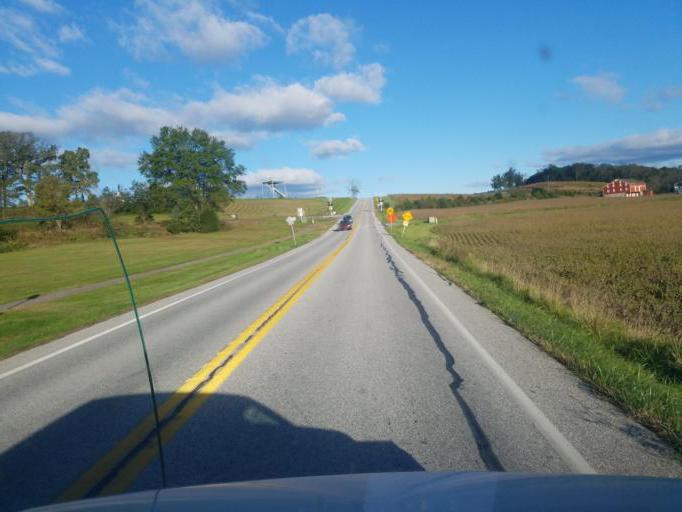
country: US
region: Pennsylvania
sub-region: Adams County
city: Gettysburg
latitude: 39.8428
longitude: -77.2399
